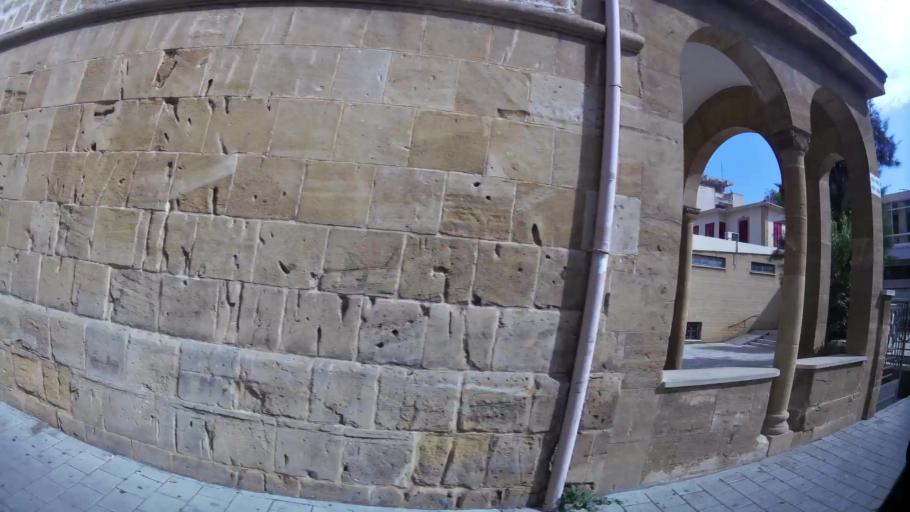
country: CY
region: Lefkosia
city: Nicosia
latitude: 35.1714
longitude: 33.3633
